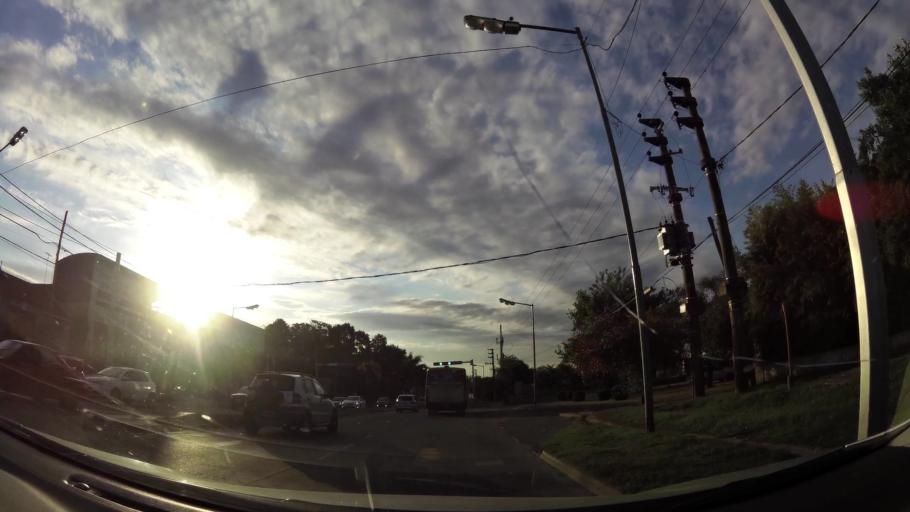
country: AR
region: Buenos Aires
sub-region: Partido de Tigre
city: Tigre
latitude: -34.4512
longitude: -58.6570
